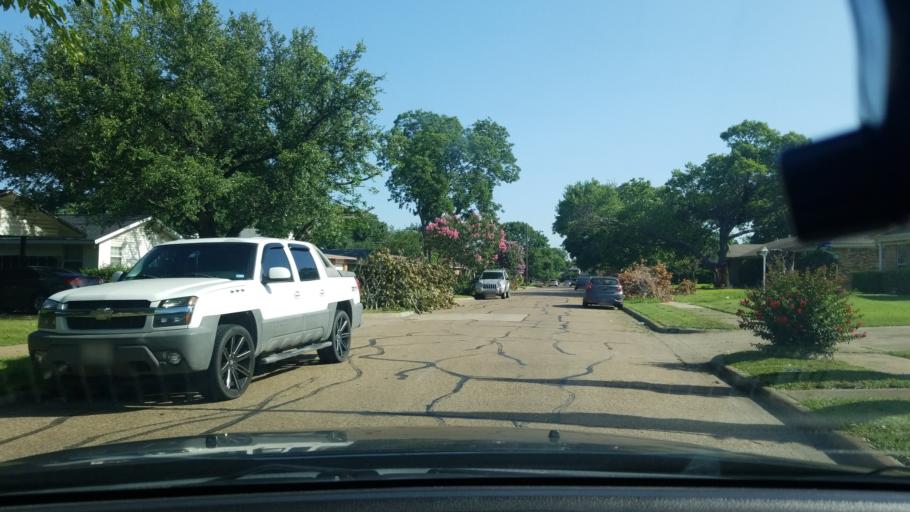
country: US
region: Texas
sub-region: Dallas County
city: Mesquite
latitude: 32.8077
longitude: -96.6803
